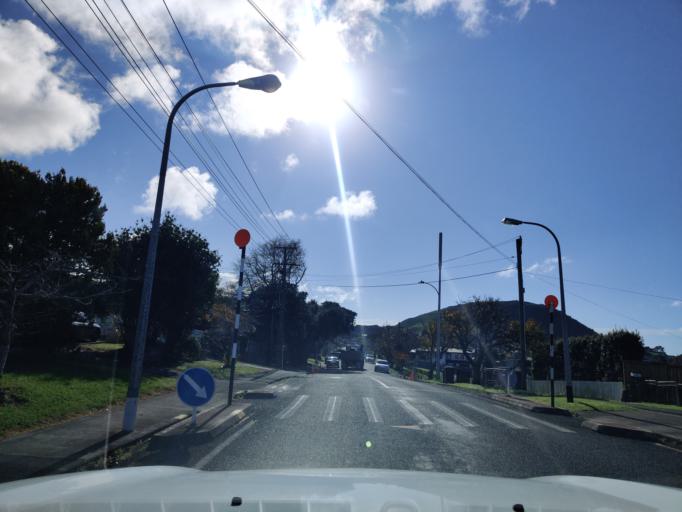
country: NZ
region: Auckland
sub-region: Auckland
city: Tamaki
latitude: -36.8995
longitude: 174.8390
